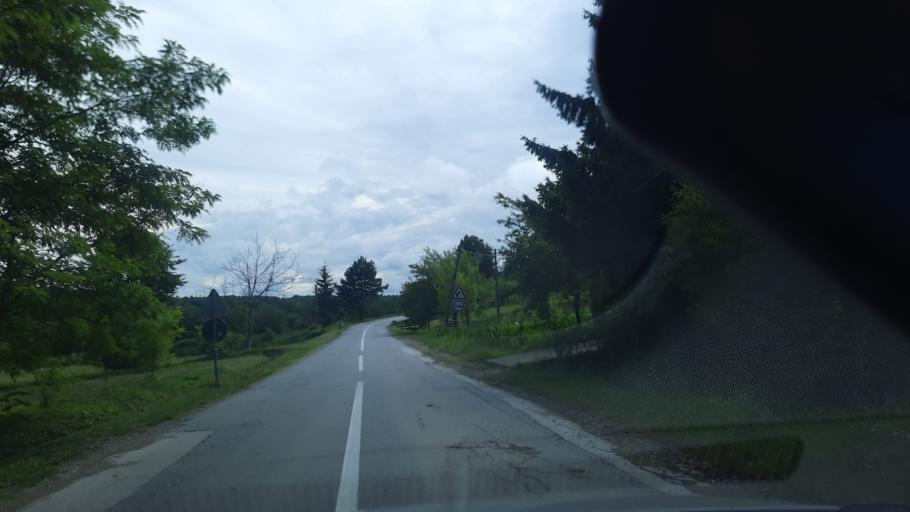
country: RS
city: Glozan
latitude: 45.1366
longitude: 19.5804
